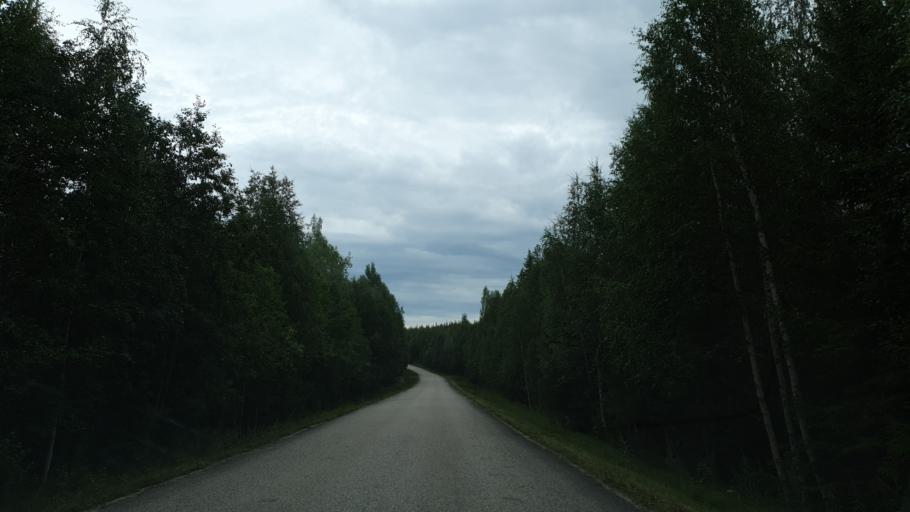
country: FI
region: Kainuu
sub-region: Kehys-Kainuu
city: Kuhmo
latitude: 64.3528
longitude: 29.0827
